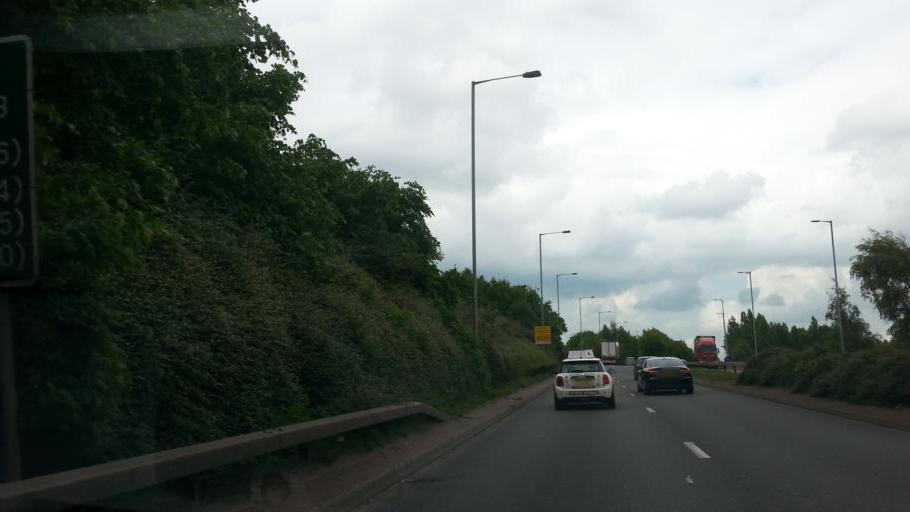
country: GB
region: England
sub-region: Wolverhampton
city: Bilston
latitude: 52.5668
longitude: -2.0634
